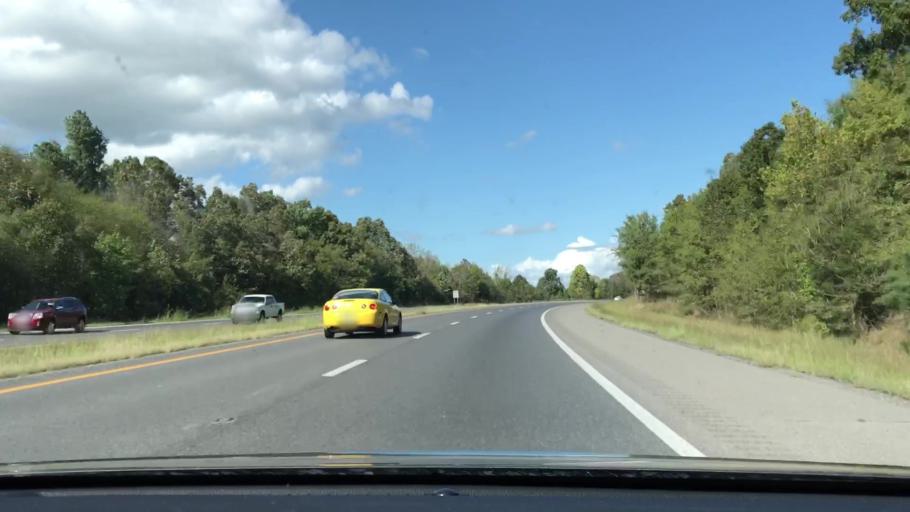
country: US
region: Kentucky
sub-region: Marshall County
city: Benton
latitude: 36.9207
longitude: -88.3513
